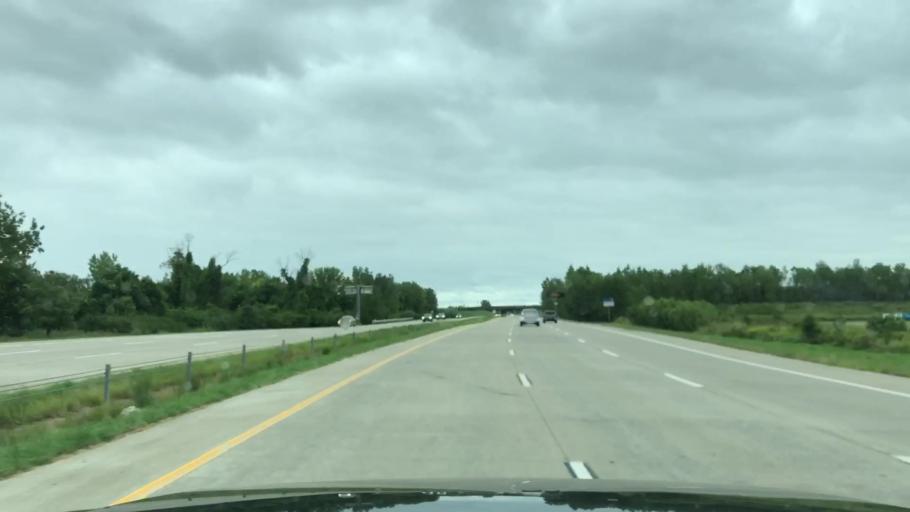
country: US
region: Missouri
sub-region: Saint Louis County
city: Maryland Heights
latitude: 38.6996
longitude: -90.5032
